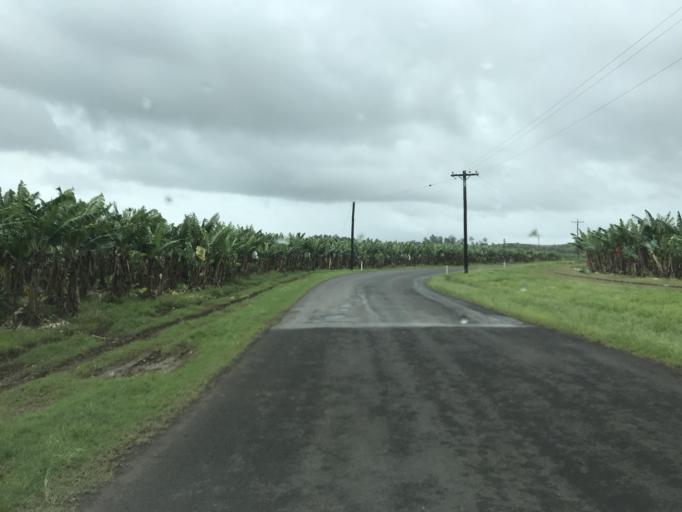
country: AU
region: Queensland
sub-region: Cassowary Coast
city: Innisfail
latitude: -17.5104
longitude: 145.9790
